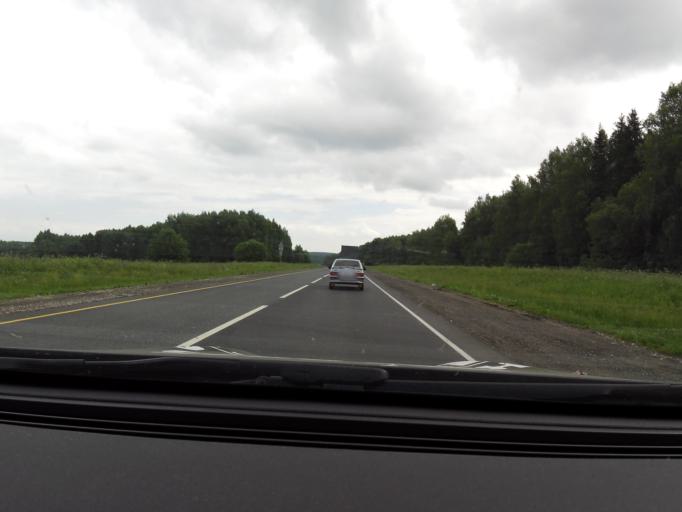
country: RU
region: Perm
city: Suksun
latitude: 57.1494
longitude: 57.2792
